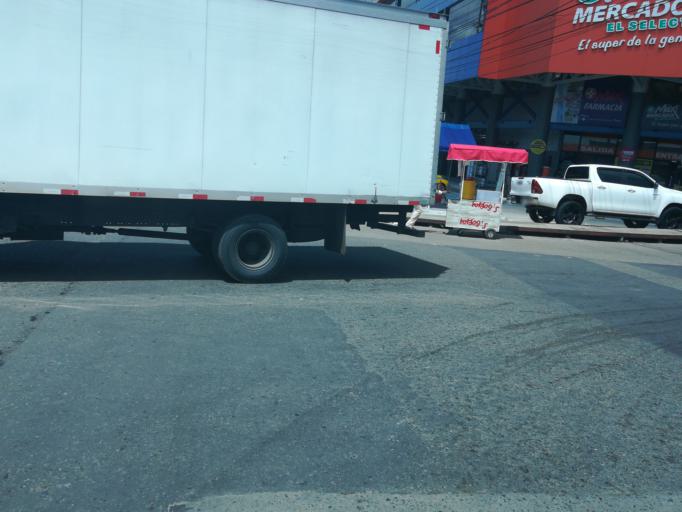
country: PA
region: Panama
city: Tocumen
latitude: 9.0799
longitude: -79.4037
